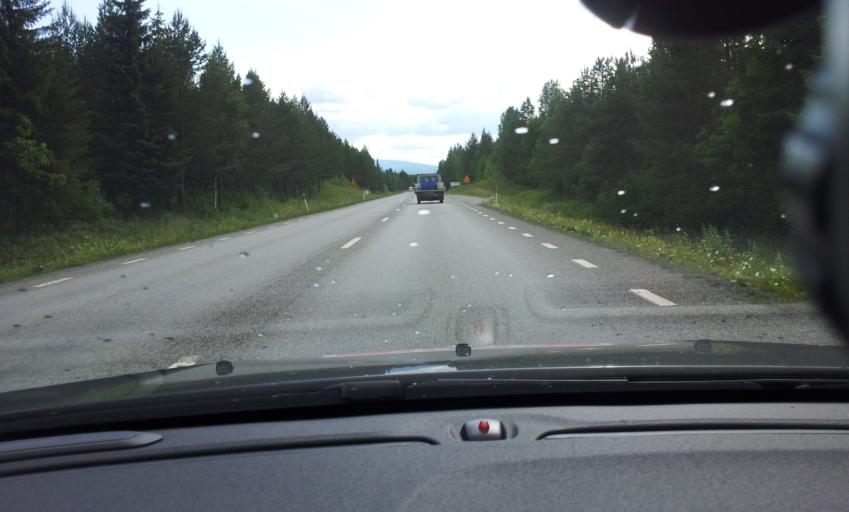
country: SE
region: Jaemtland
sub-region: Krokoms Kommun
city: Valla
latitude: 63.3169
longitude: 13.9343
